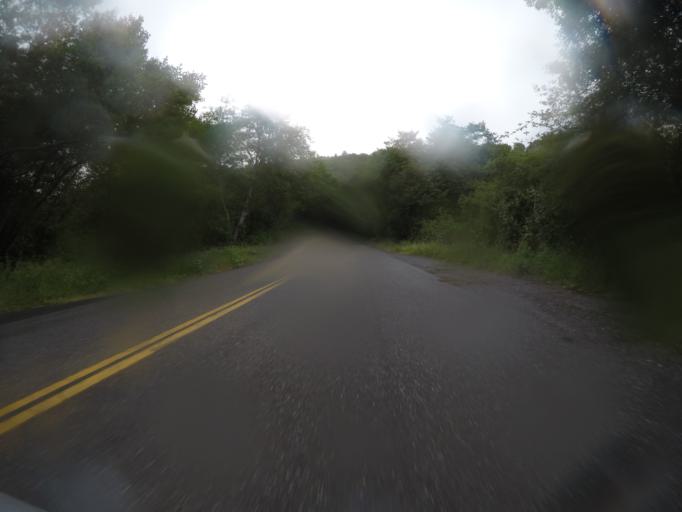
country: US
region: California
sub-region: Humboldt County
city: Westhaven-Moonstone
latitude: 41.3011
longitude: -124.0466
